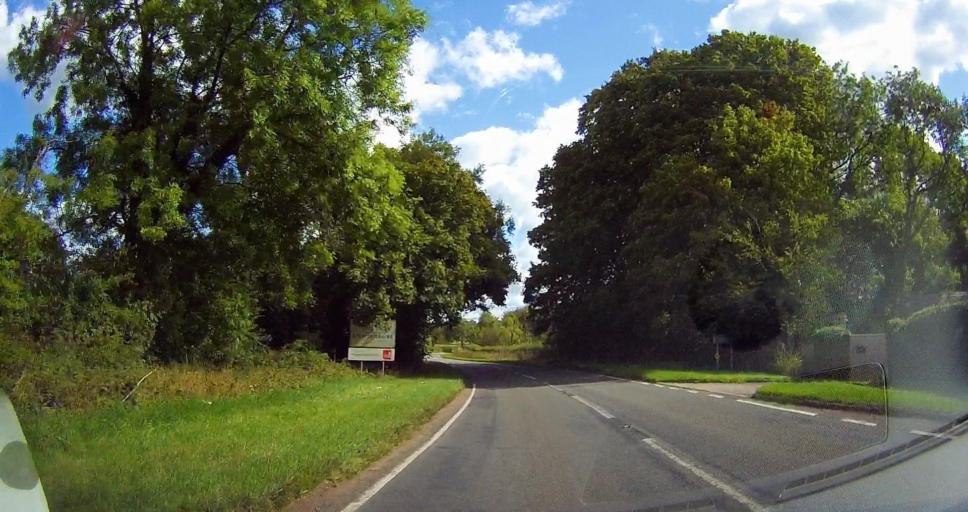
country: GB
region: England
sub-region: Cheshire East
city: Chorlton
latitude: 52.9610
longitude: -2.3849
